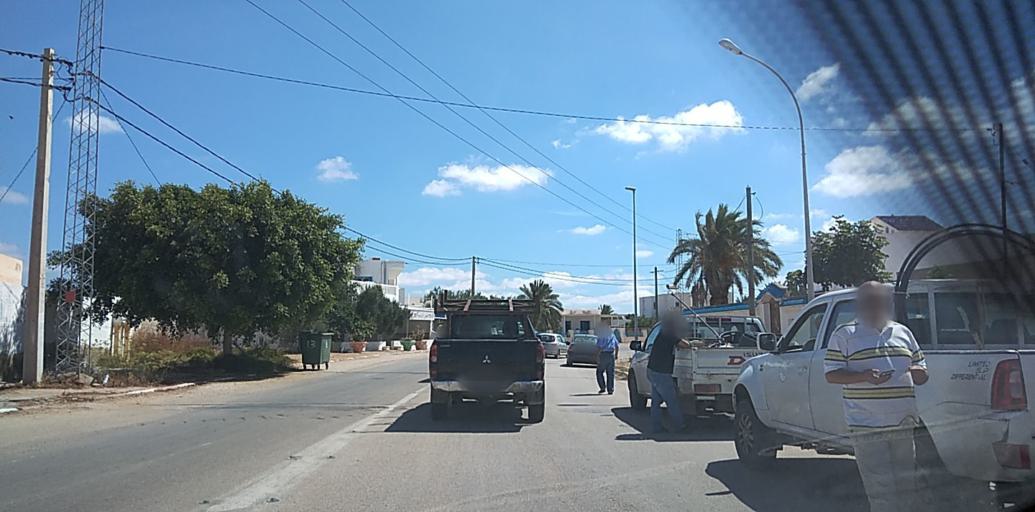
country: TN
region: Safaqis
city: Al Qarmadah
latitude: 34.6730
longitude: 11.1399
